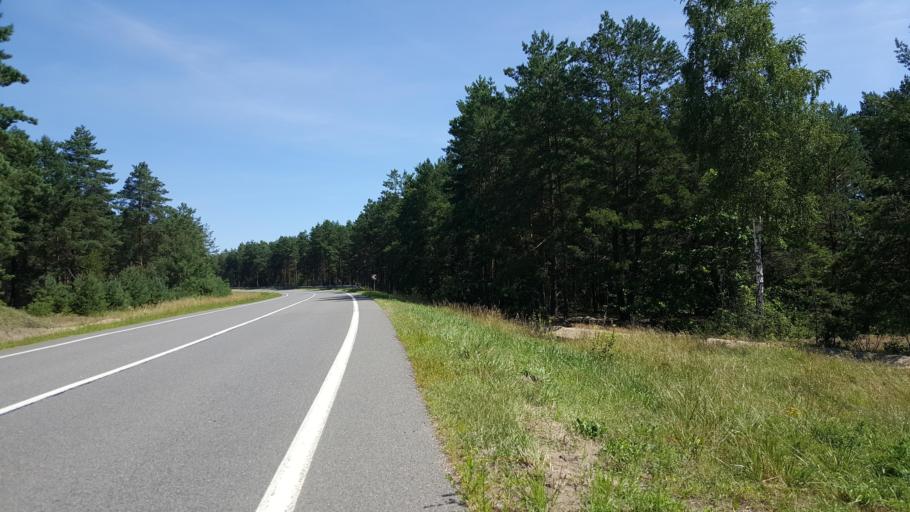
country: BY
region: Brest
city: Zhabinka
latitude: 52.4682
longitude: 24.1520
